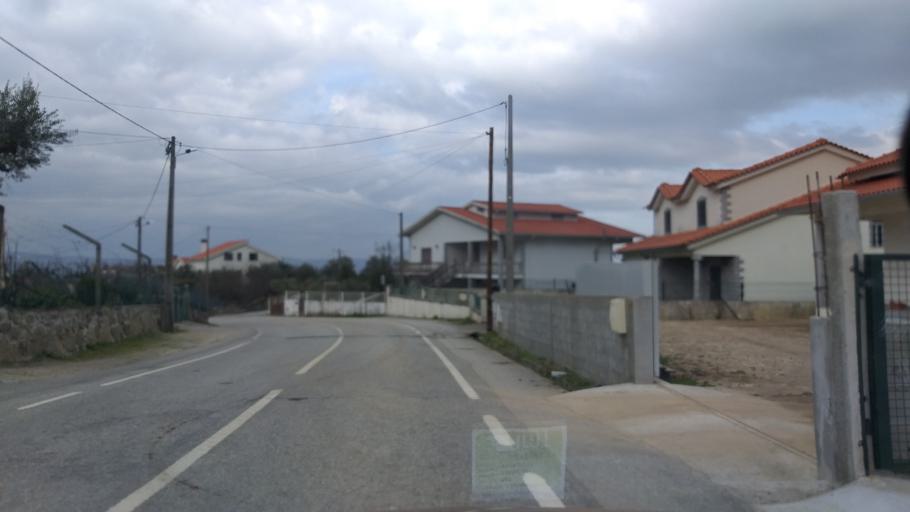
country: PT
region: Guarda
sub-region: Seia
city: Seia
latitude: 40.4906
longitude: -7.6313
